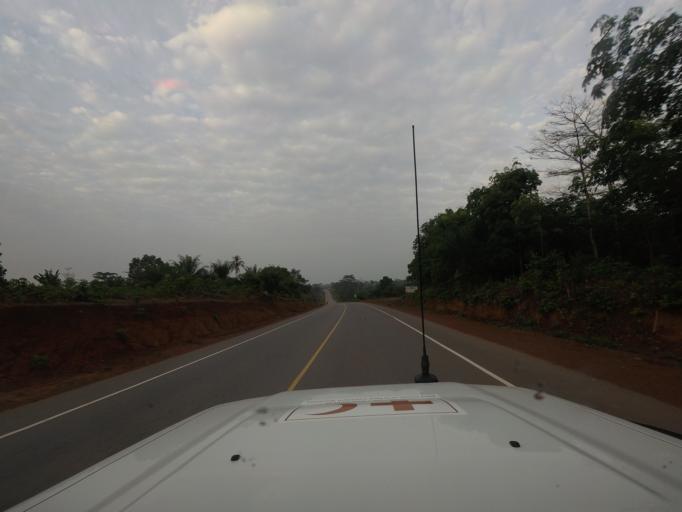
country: LR
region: Nimba
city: Sanniquellie
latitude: 7.2033
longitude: -9.0169
